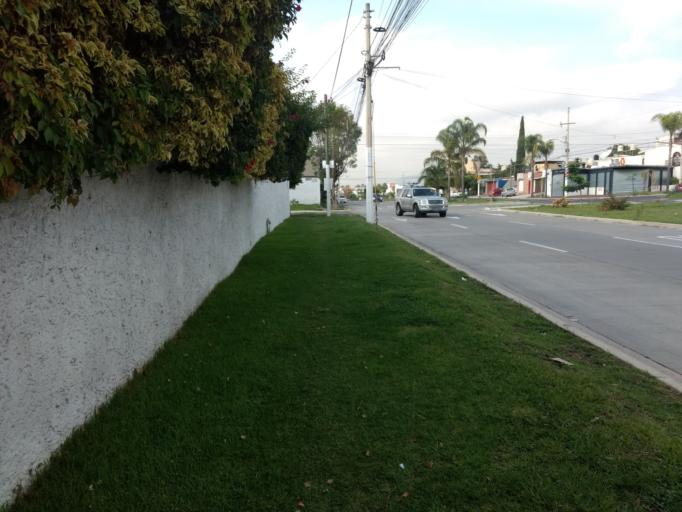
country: MX
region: Jalisco
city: Guadalajara
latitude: 20.6665
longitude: -103.4362
